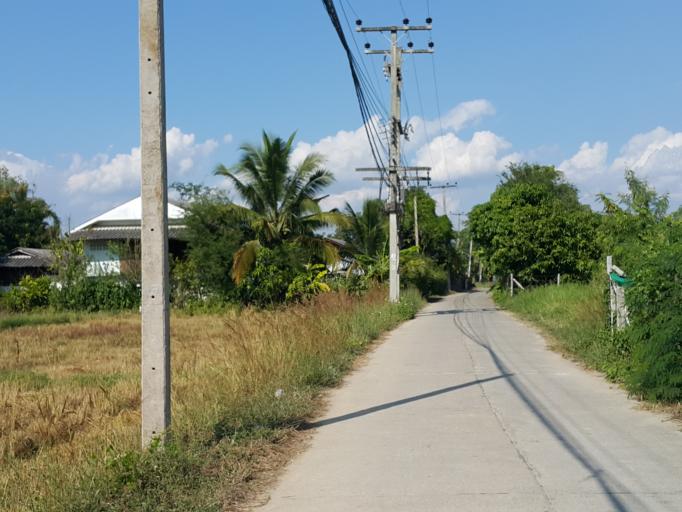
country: TH
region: Chiang Mai
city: San Sai
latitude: 18.8001
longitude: 99.0700
